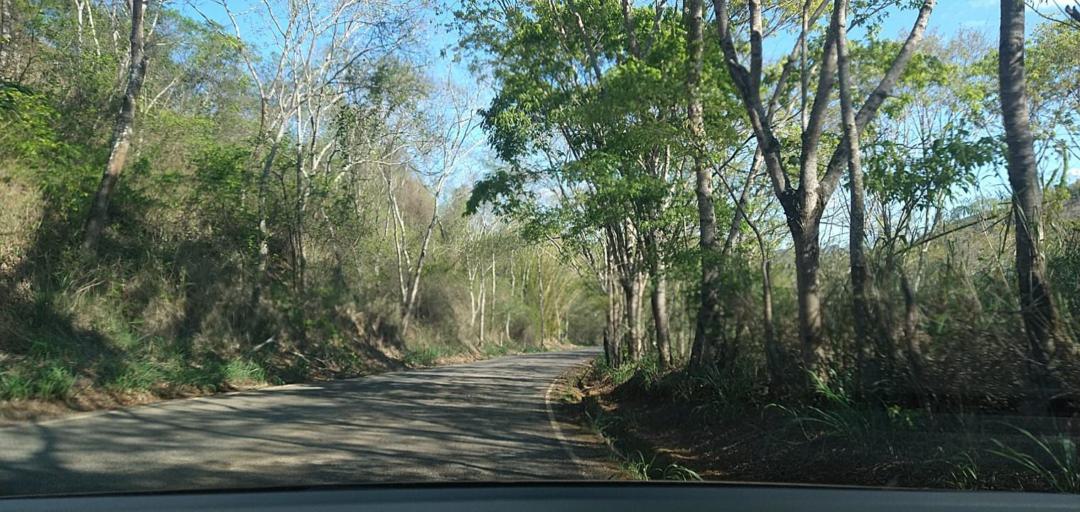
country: BR
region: Minas Gerais
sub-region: Ponte Nova
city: Ponte Nova
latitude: -20.2416
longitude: -42.8955
